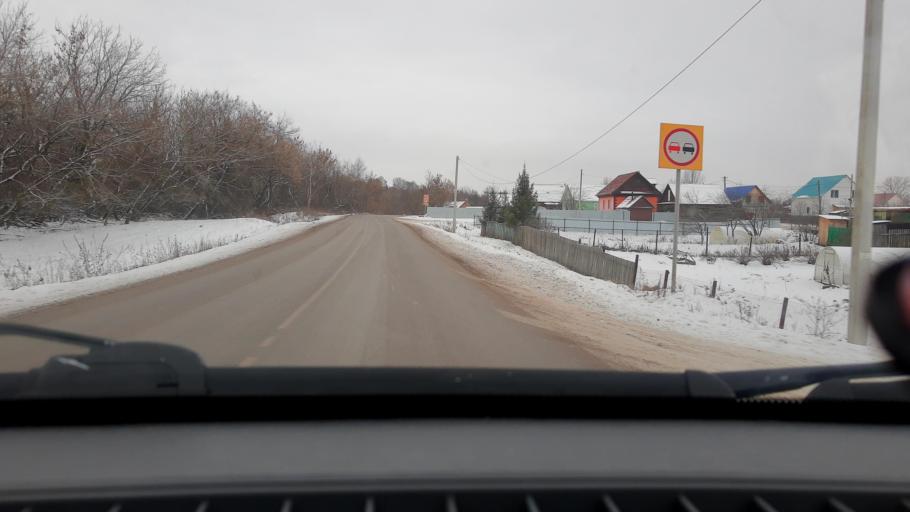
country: RU
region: Bashkortostan
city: Iglino
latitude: 54.8417
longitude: 56.4521
